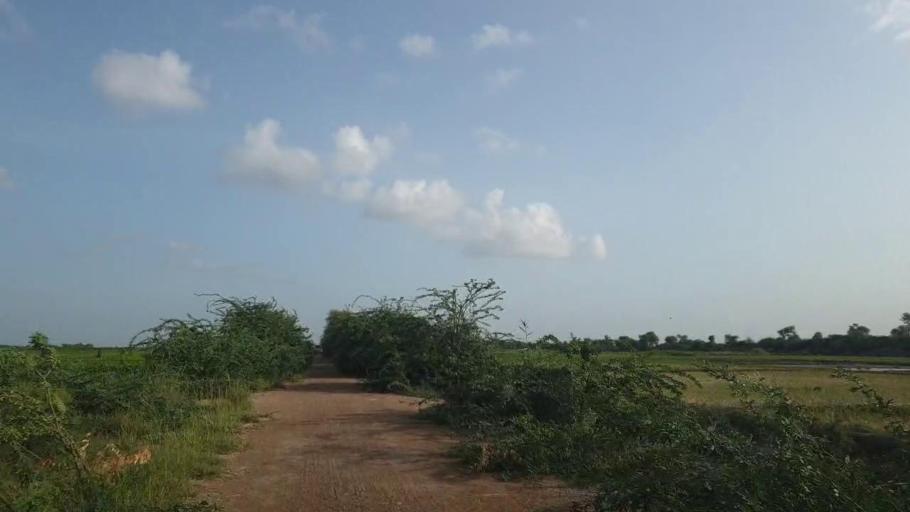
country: PK
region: Sindh
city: Kadhan
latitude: 24.6363
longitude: 69.1050
